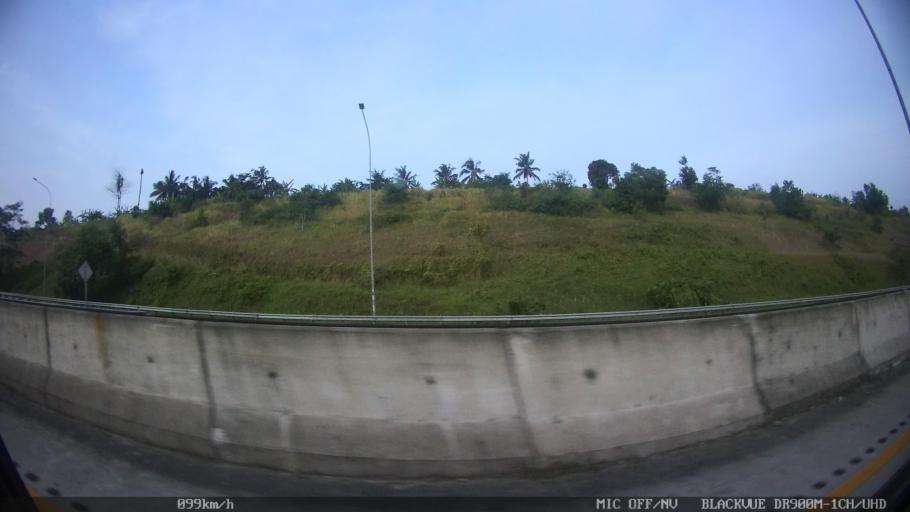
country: ID
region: Lampung
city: Penengahan
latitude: -5.8129
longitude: 105.7354
